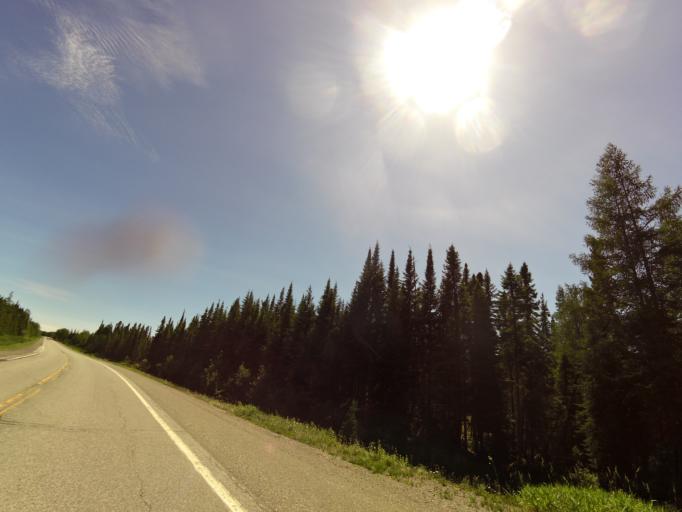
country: CA
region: Quebec
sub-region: Nord-du-Quebec
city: Lebel-sur-Quevillon
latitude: 48.8169
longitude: -77.1273
